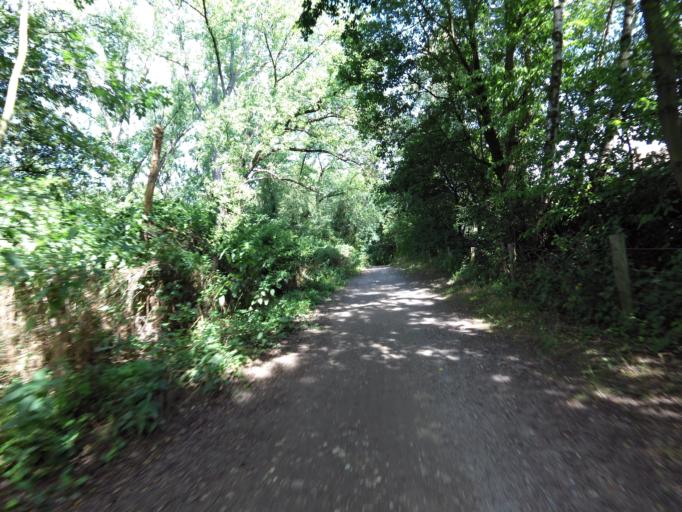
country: NL
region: Limburg
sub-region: Gemeente Kerkrade
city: Kerkrade
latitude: 50.8909
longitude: 6.0770
